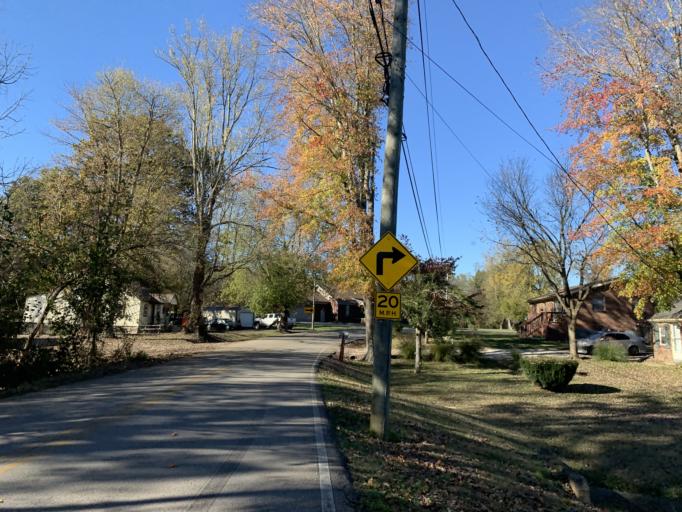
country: US
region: Kentucky
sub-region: Jefferson County
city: Pleasure Ridge Park
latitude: 38.1530
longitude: -85.8779
